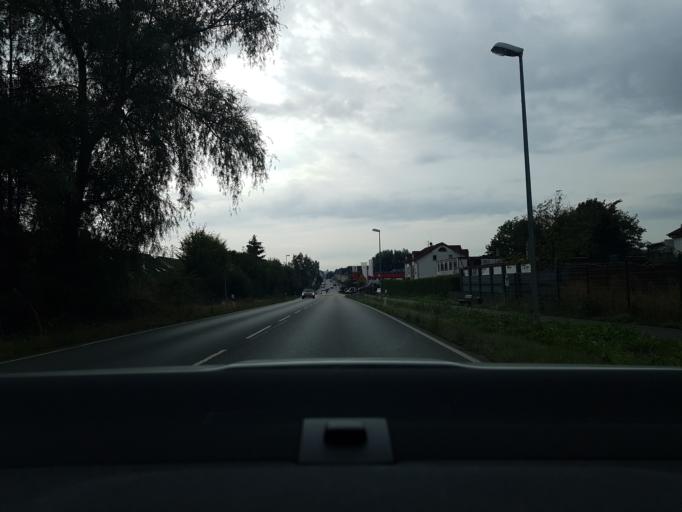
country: DE
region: Hesse
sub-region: Regierungsbezirk Giessen
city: Limburg an der Lahn
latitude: 50.3721
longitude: 8.0832
